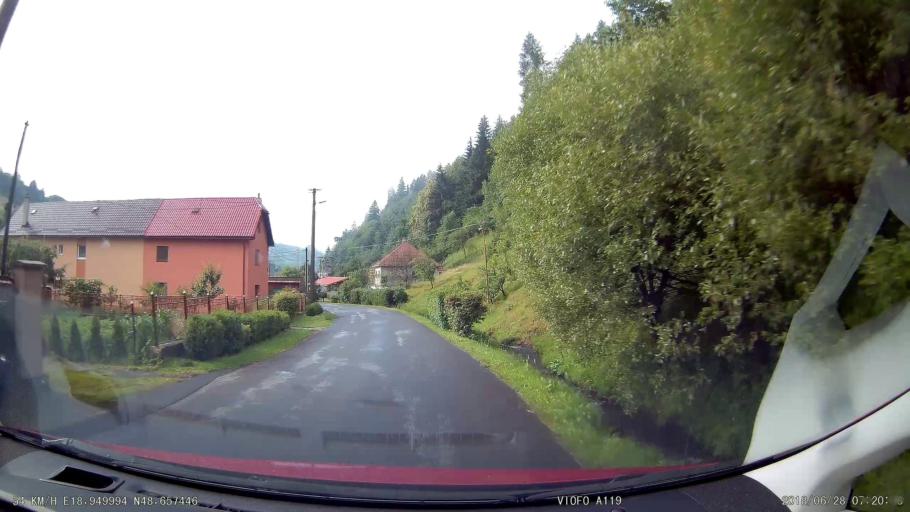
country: SK
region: Banskobystricky
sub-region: Okres Ziar nad Hronom
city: Kremnica
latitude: 48.6572
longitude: 18.9501
